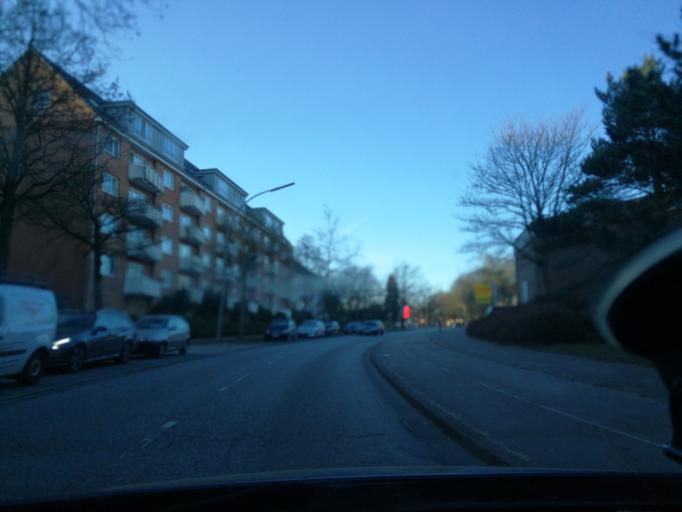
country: DE
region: Hamburg
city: Harburg
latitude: 53.4577
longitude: 9.9563
